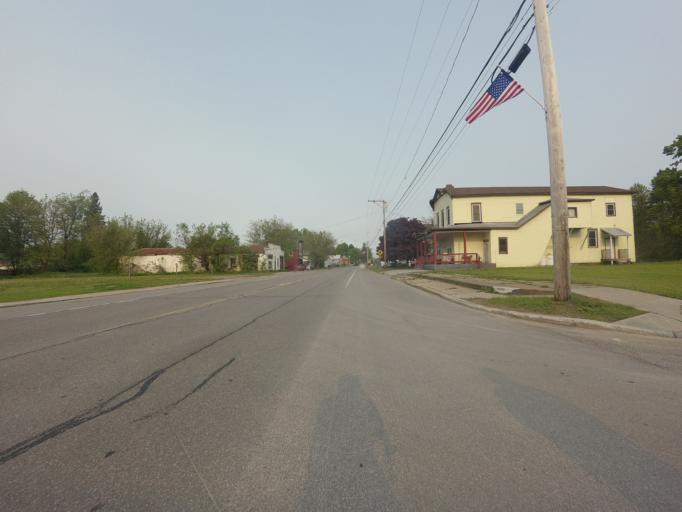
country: US
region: New York
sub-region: Jefferson County
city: Carthage
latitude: 44.0691
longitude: -75.4940
